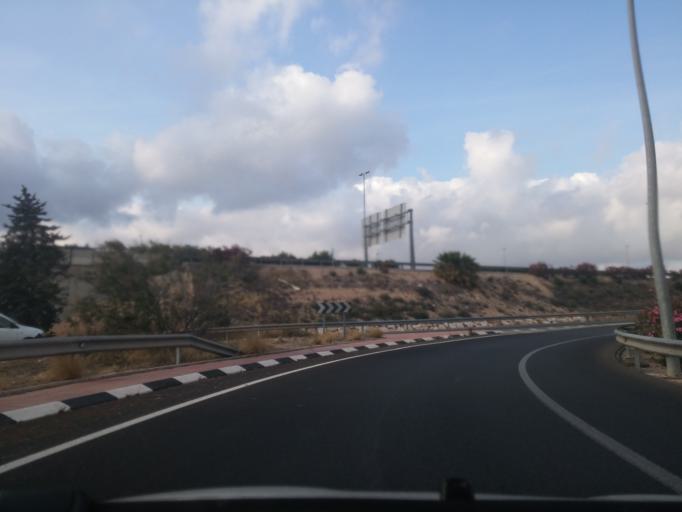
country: ES
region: Valencia
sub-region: Provincia de Alicante
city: San Vicent del Raspeig
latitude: 38.3793
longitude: -0.5127
